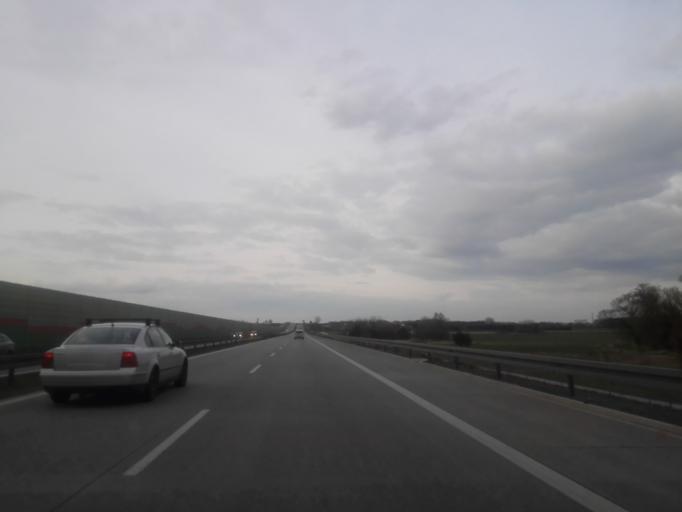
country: PL
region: Lodz Voivodeship
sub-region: Powiat tomaszowski
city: Tomaszow Mazowiecki
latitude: 51.5330
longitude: 19.9529
